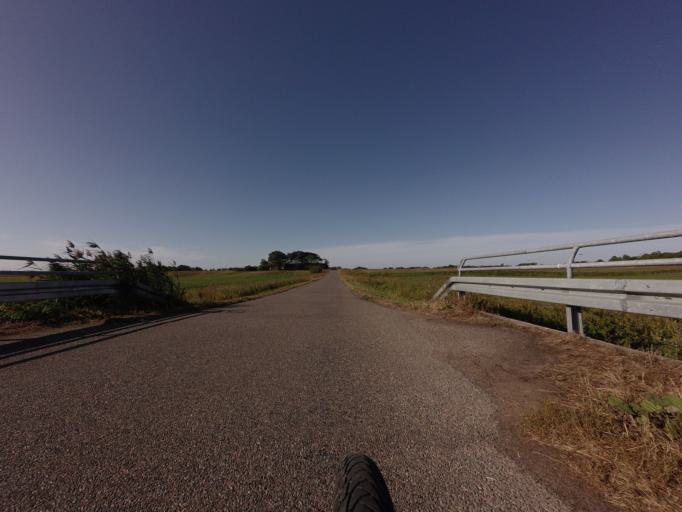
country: DK
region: North Denmark
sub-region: Hjorring Kommune
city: Vra
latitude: 57.3768
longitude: 9.9568
